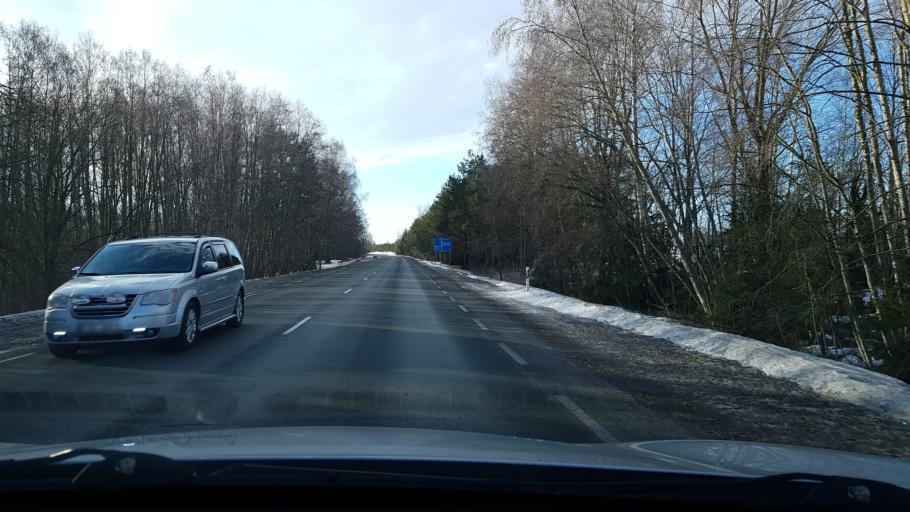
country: EE
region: Viljandimaa
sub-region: Vohma linn
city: Vohma
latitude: 58.5347
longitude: 25.5919
